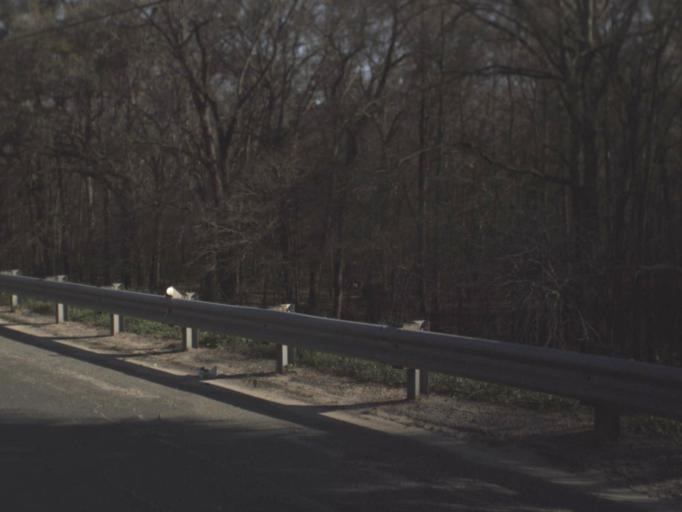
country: US
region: Florida
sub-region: Jackson County
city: Marianna
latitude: 30.7726
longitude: -85.2148
